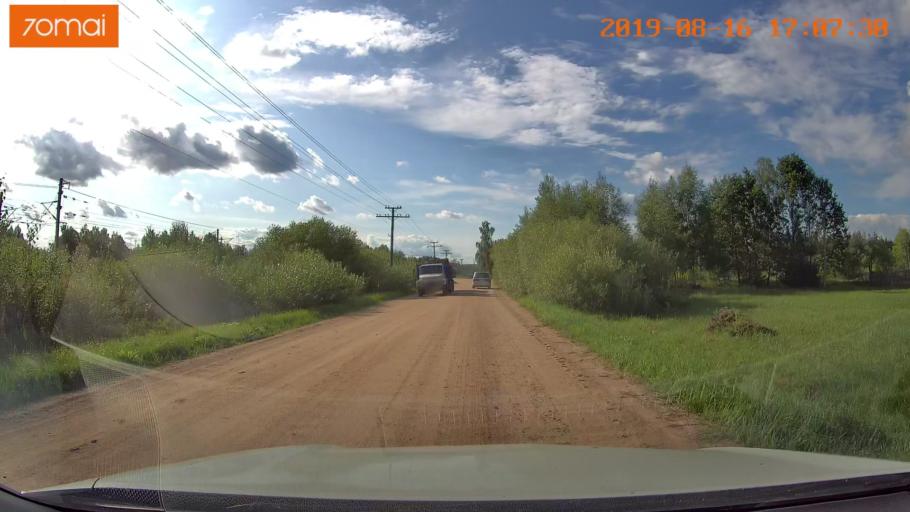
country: BY
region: Mogilev
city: Hlusha
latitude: 53.2217
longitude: 28.9241
